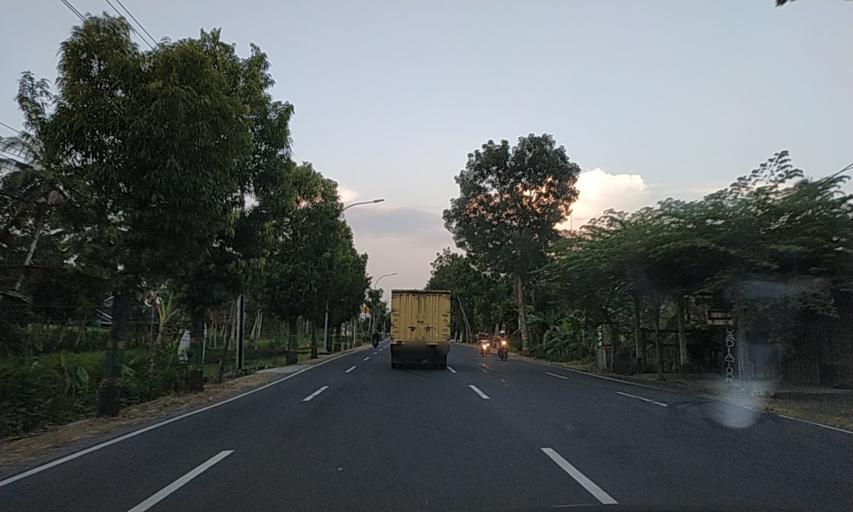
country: ID
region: Daerah Istimewa Yogyakarta
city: Srandakan
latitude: -7.8757
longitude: 110.1350
